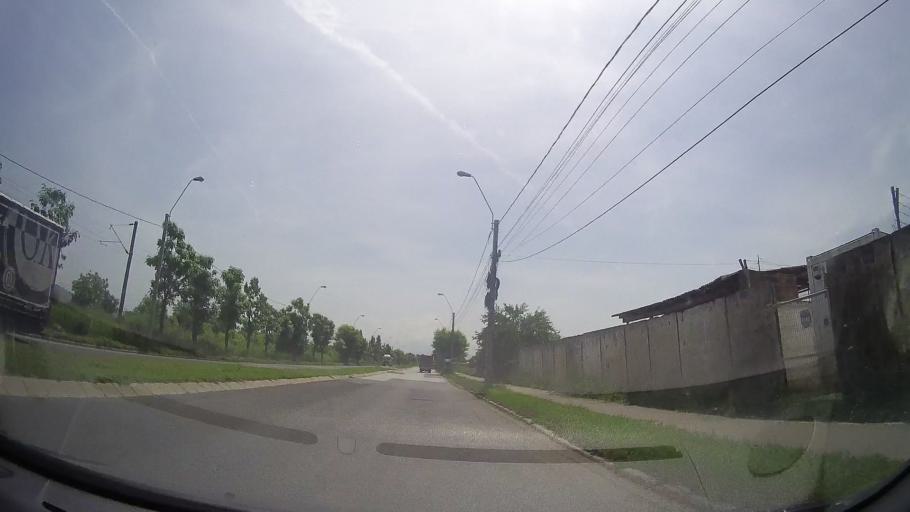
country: RO
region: Hunedoara
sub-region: Municipiul Deva
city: Deva
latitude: 45.8946
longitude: 22.8998
